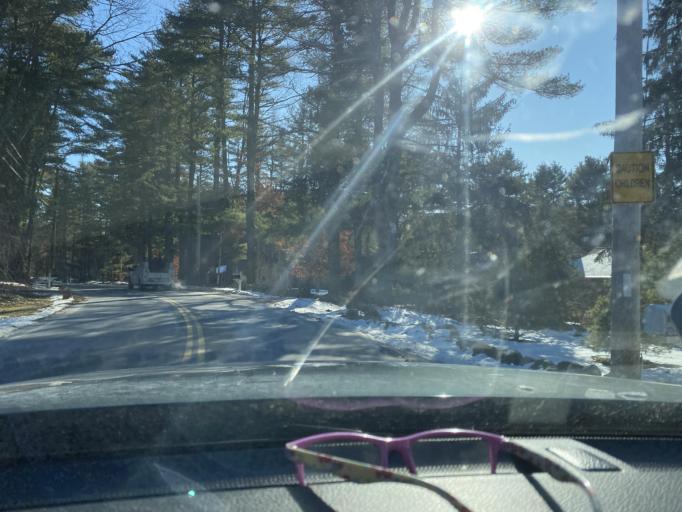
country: US
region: Massachusetts
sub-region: Norfolk County
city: Walpole
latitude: 42.1661
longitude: -71.2620
